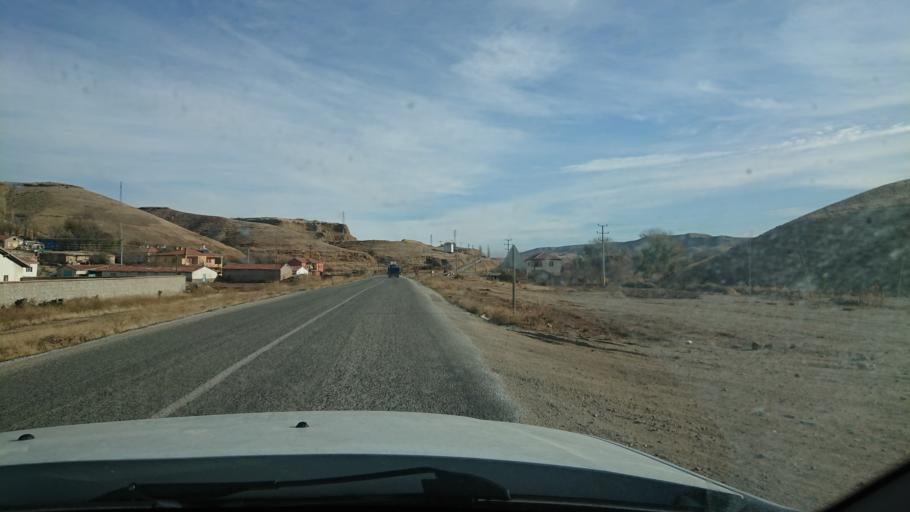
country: TR
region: Aksaray
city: Acipinar
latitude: 38.4842
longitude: 33.9100
